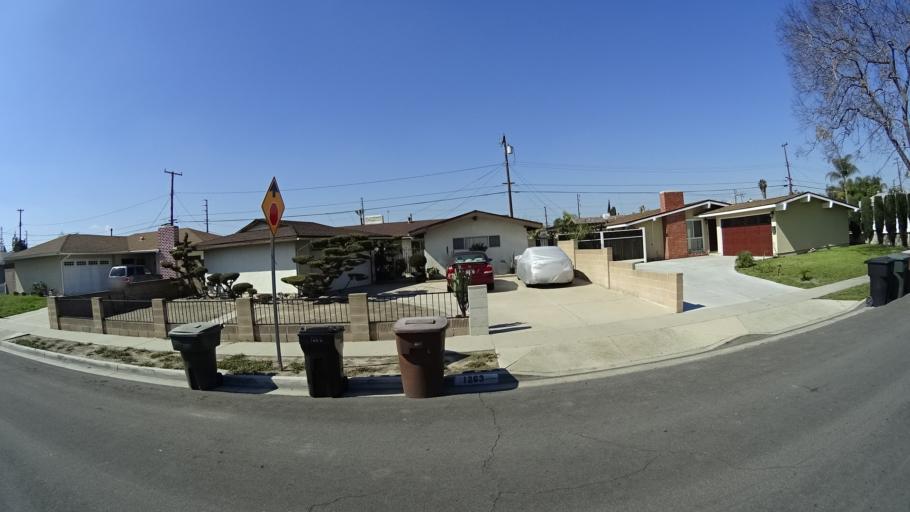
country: US
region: California
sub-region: Orange County
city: Buena Park
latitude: 33.8514
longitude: -117.9662
